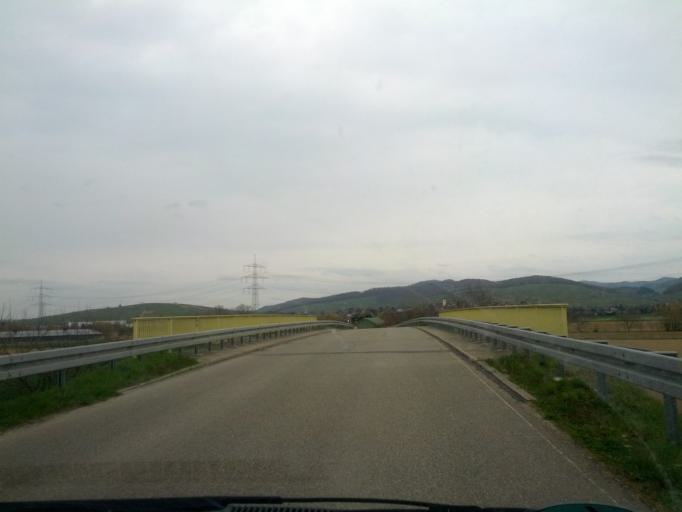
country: DE
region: Baden-Wuerttemberg
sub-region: Freiburg Region
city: Bad Krozingen
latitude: 47.9116
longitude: 7.7190
